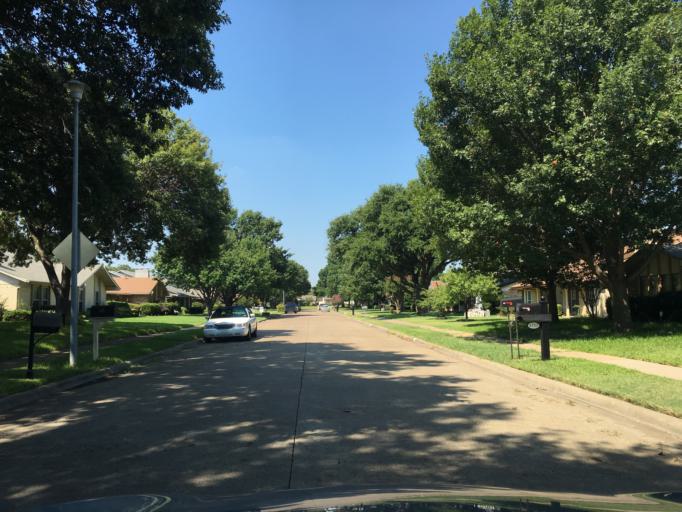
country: US
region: Texas
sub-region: Dallas County
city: Garland
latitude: 32.9365
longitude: -96.6536
